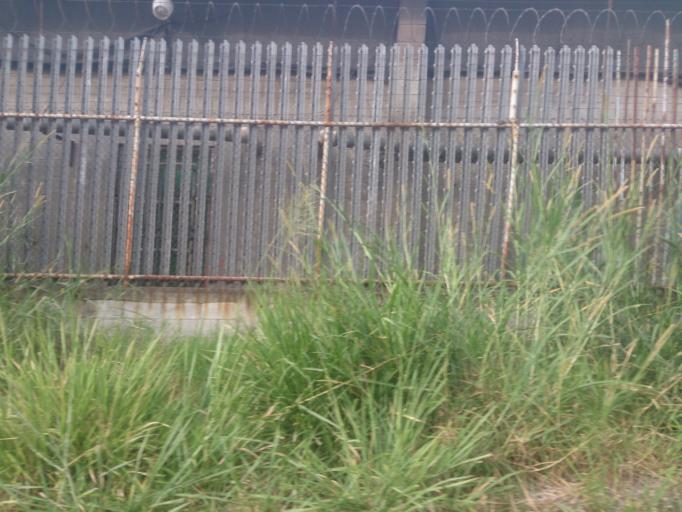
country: CR
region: San Jose
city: San Rafael
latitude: 9.9401
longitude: -84.1223
